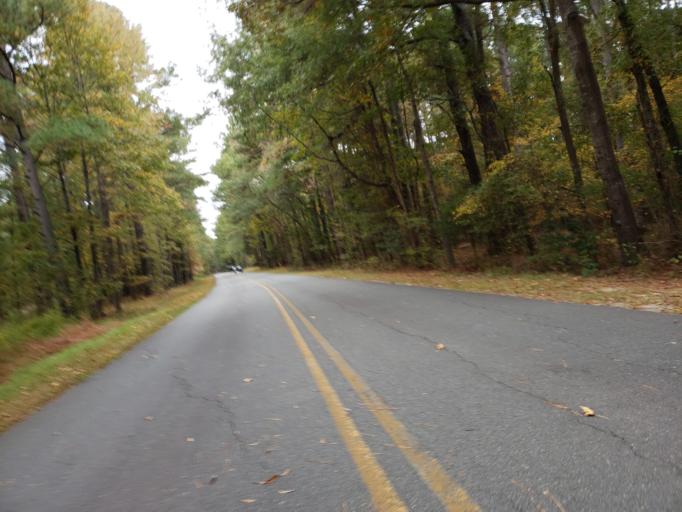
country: US
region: North Carolina
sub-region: Chatham County
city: Fearrington Village
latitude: 35.7517
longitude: -79.0418
